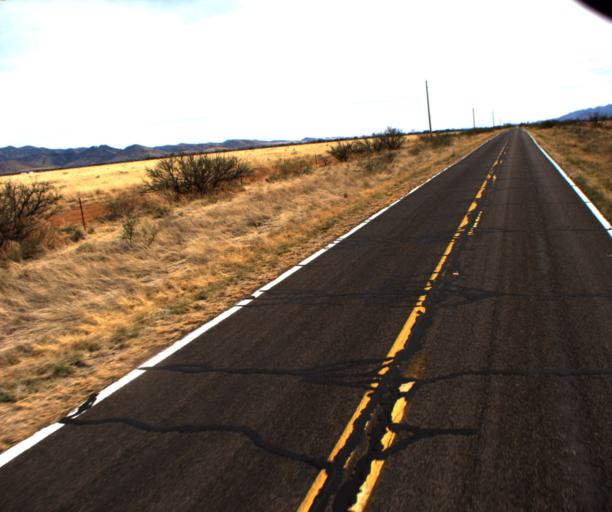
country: US
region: Arizona
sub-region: Cochise County
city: Willcox
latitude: 31.9050
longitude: -109.4914
